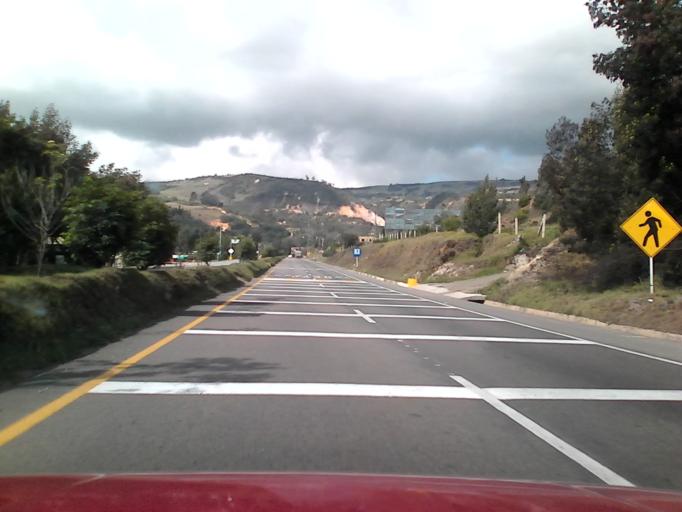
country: CO
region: Boyaca
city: Combita
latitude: 5.6166
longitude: -73.3171
